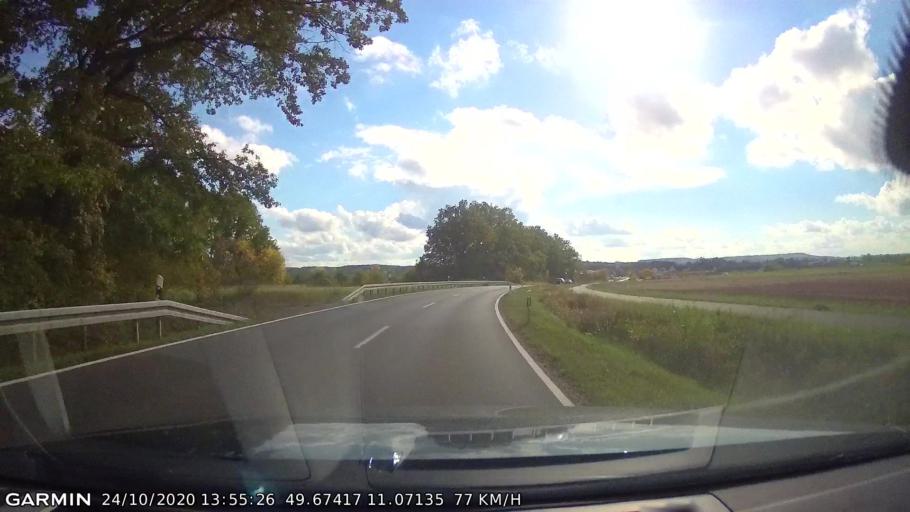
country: DE
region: Bavaria
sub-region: Upper Franconia
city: Poxdorf
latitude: 49.6740
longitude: 11.0714
